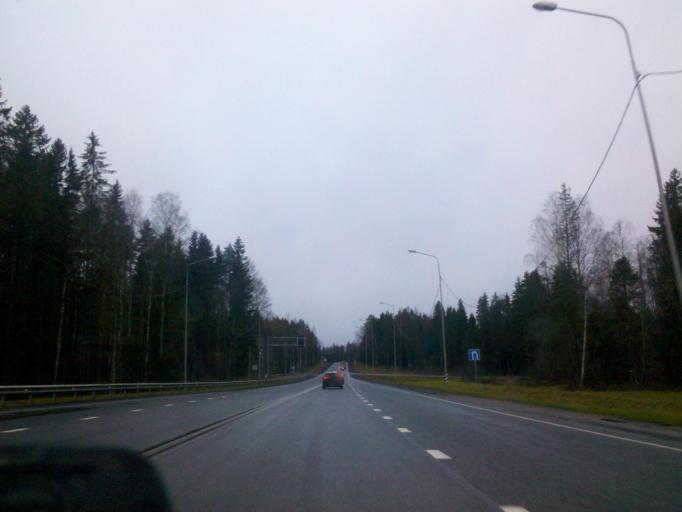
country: RU
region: Republic of Karelia
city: Shuya
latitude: 61.8180
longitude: 34.1271
